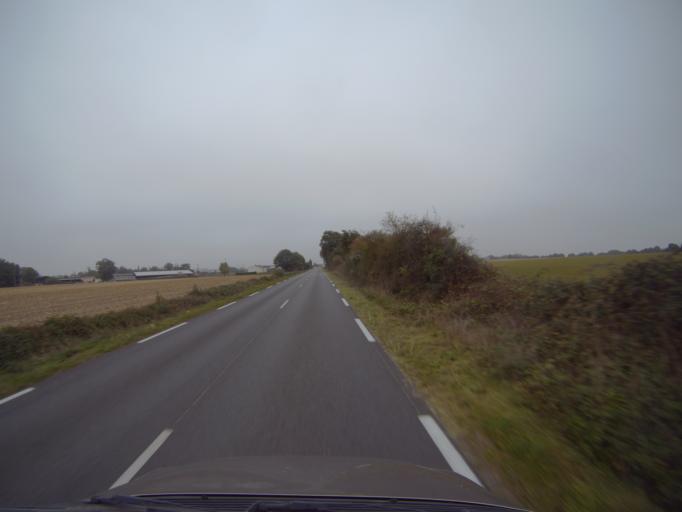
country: FR
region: Pays de la Loire
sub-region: Departement de la Vendee
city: Cugand
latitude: 47.0511
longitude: -1.2524
